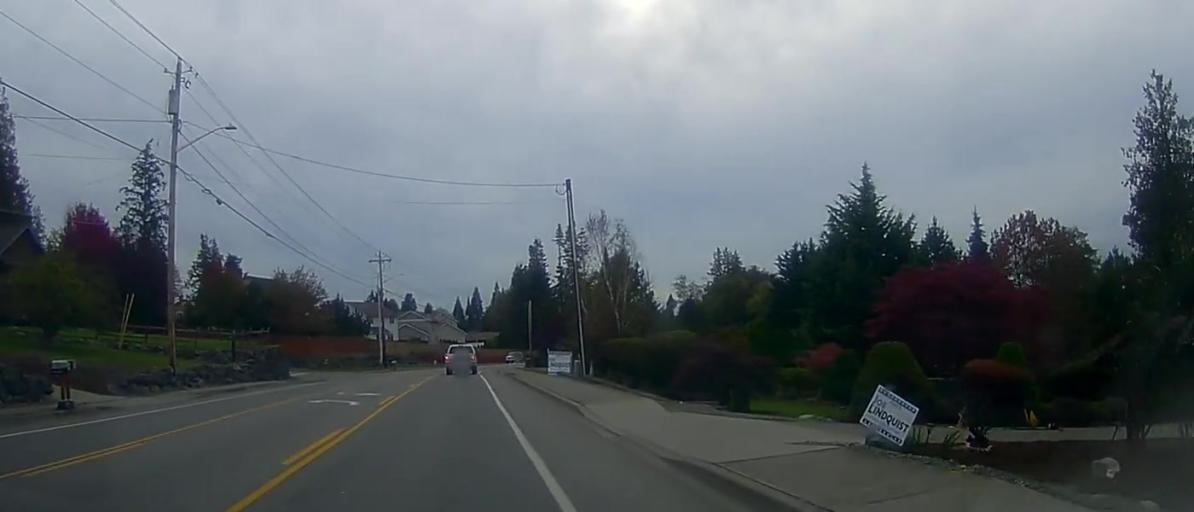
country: US
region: Washington
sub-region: Skagit County
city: Burlington
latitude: 48.4473
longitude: -122.3088
